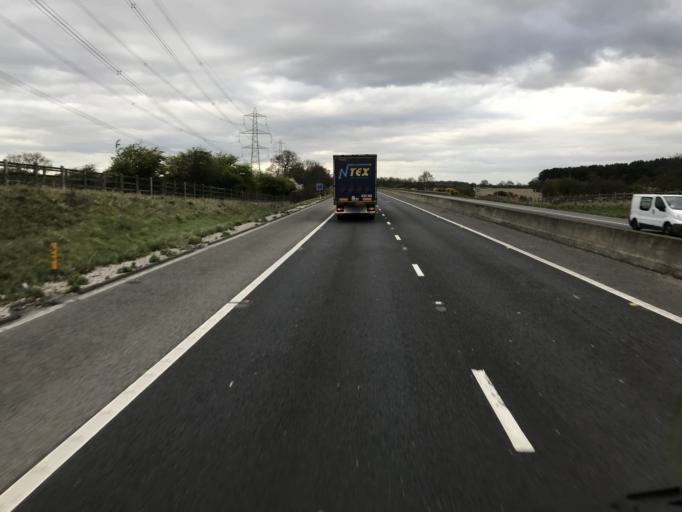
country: GB
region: England
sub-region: Doncaster
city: Cantley
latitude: 53.5095
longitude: -1.0498
